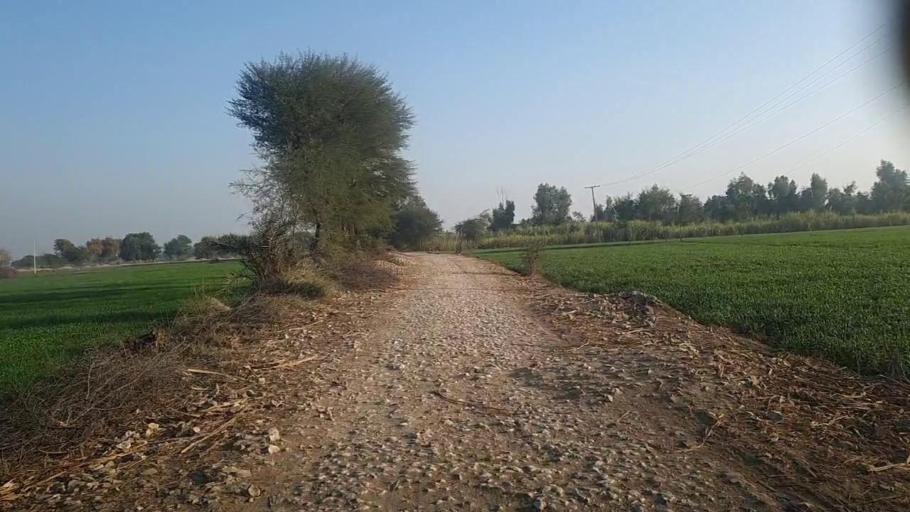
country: PK
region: Sindh
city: Khairpur
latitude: 28.0740
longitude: 69.7386
